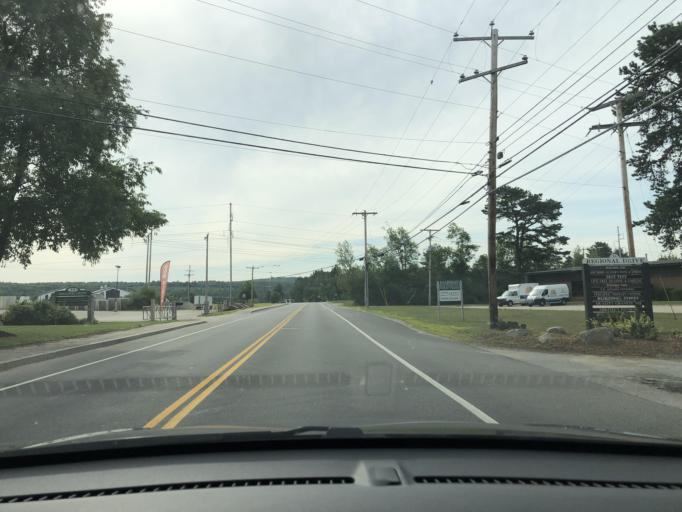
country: US
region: New Hampshire
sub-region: Merrimack County
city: Concord
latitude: 43.2089
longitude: -71.4874
